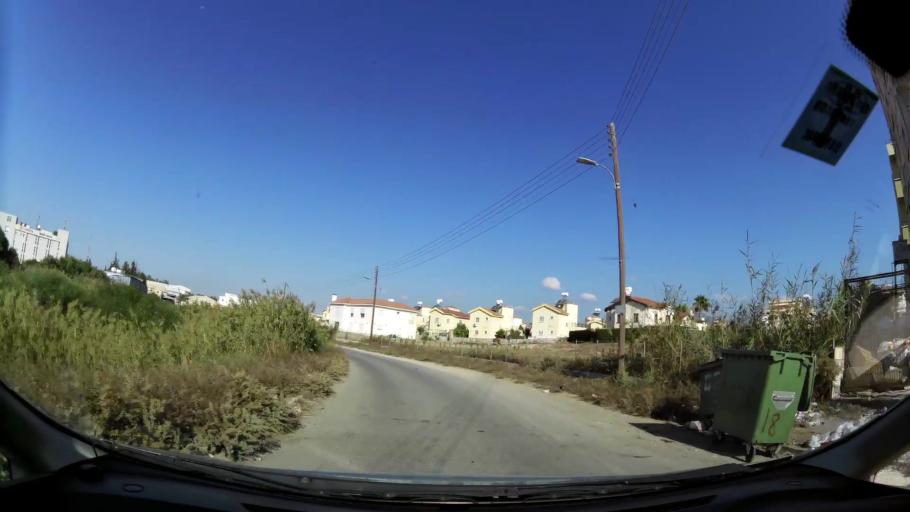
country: CY
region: Lefkosia
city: Nicosia
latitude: 35.2113
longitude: 33.3672
